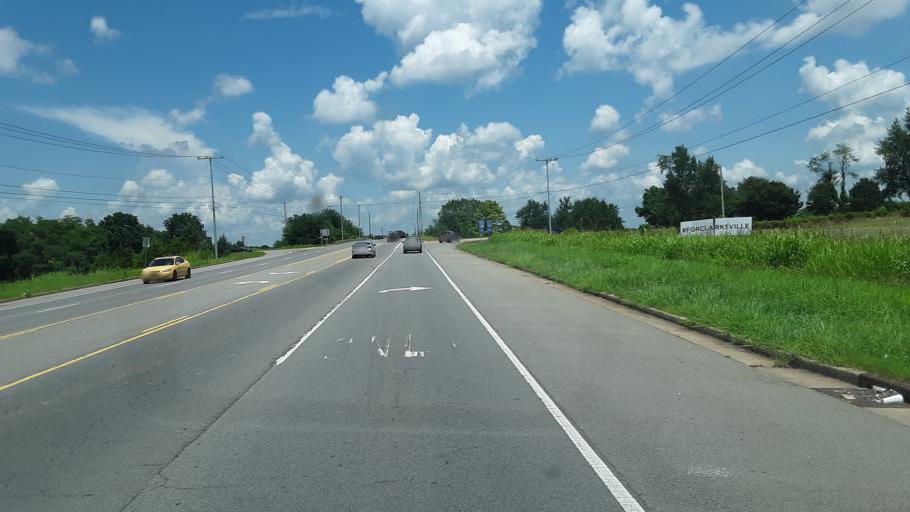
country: US
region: Tennessee
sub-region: Montgomery County
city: Clarksville
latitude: 36.6268
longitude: -87.3175
